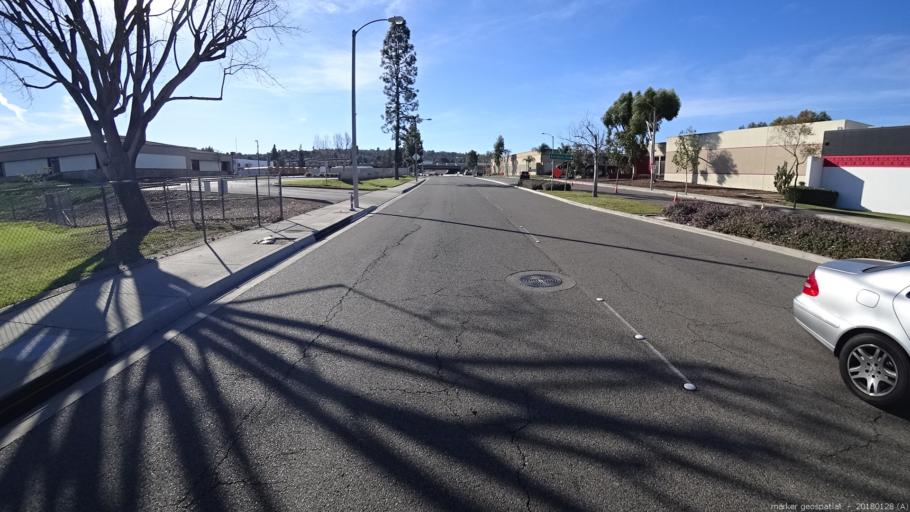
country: US
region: California
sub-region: Los Angeles County
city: Walnut
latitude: 34.0012
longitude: -117.8552
